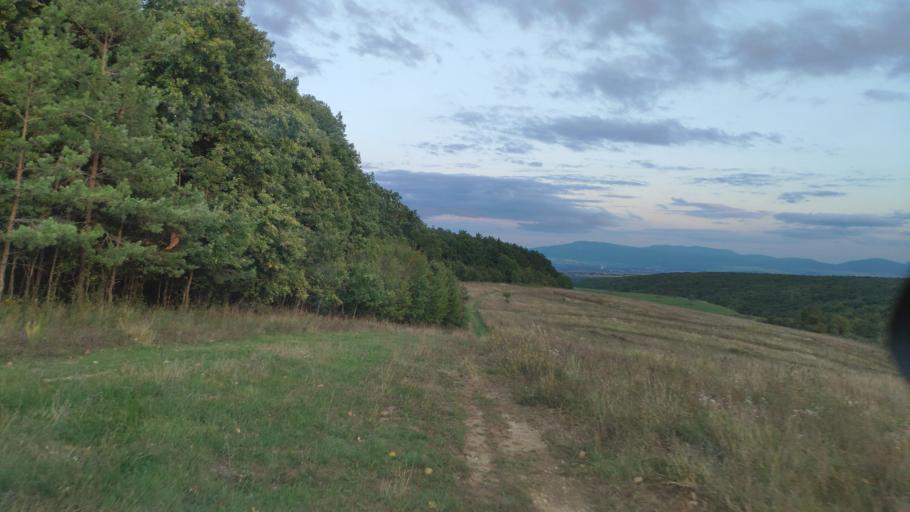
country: SK
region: Kosicky
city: Kosice
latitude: 48.7046
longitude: 21.1987
